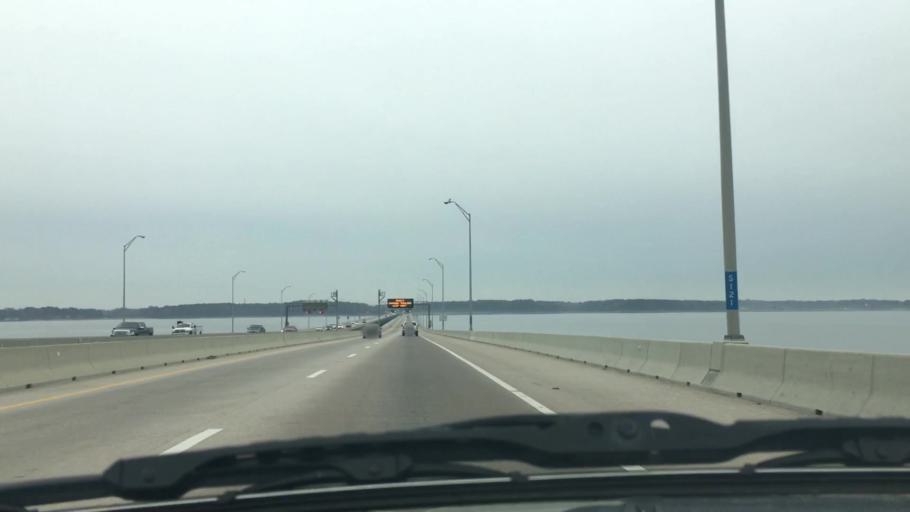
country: US
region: Virginia
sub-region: City of Newport News
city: Newport News
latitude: 36.9179
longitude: -76.4146
